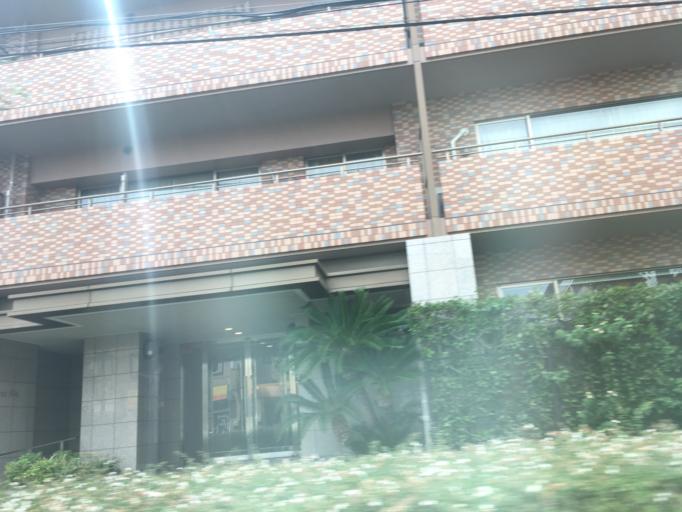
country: JP
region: Hyogo
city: Ashiya
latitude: 34.7267
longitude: 135.3188
